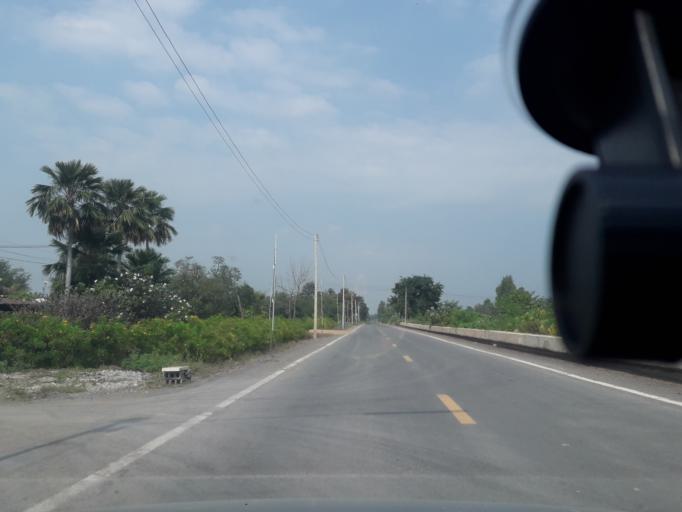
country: TH
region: Pathum Thani
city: Nong Suea
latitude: 14.2073
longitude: 100.8915
